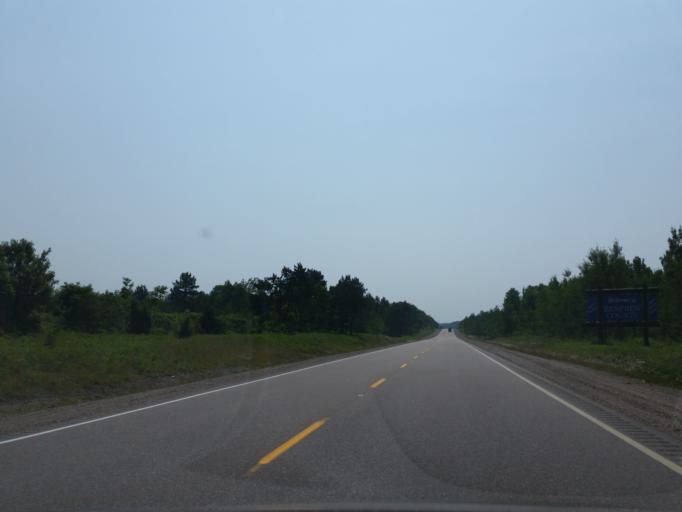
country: CA
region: Ontario
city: Mattawa
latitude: 46.2743
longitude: -78.3700
